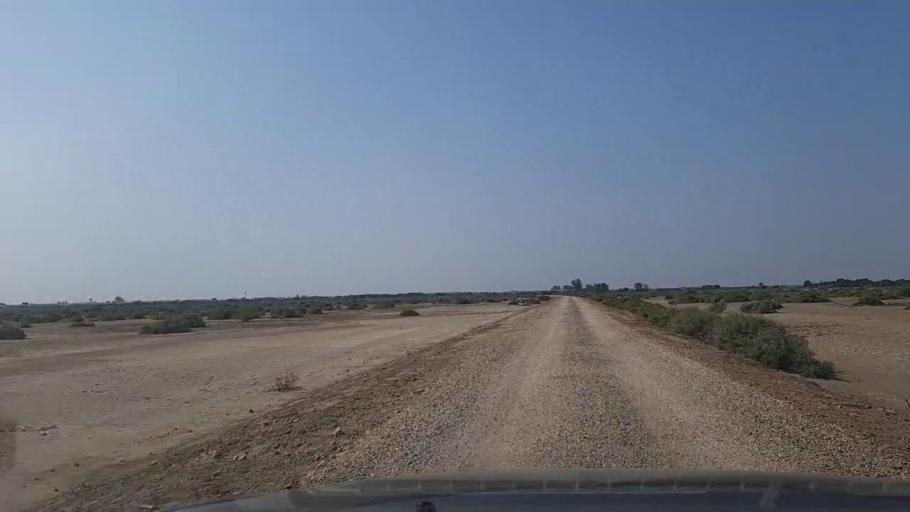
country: PK
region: Sindh
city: Mirpur Sakro
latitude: 24.4266
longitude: 67.7171
